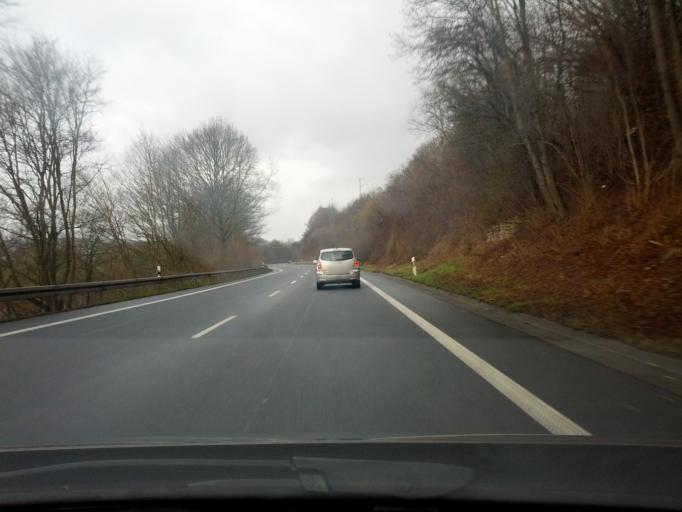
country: DE
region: Hesse
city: Witzenhausen
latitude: 51.3678
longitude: 9.8128
